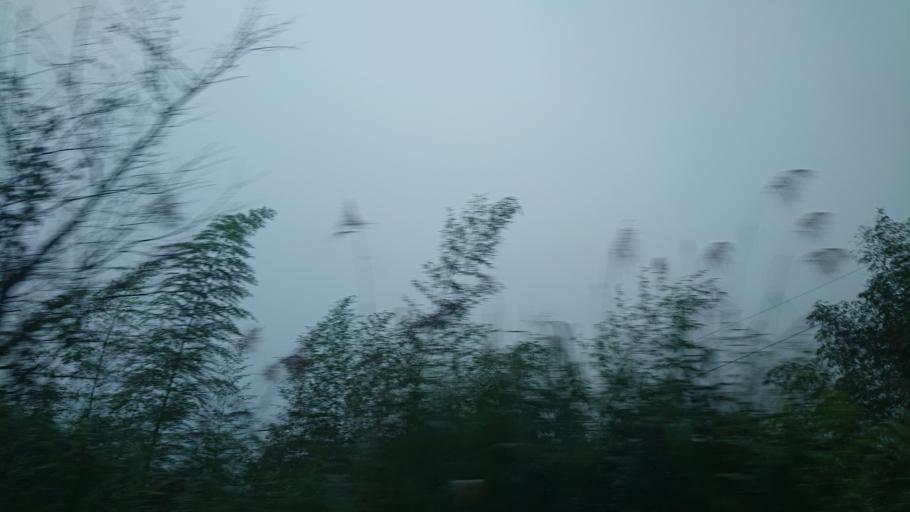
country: TW
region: Taiwan
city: Lugu
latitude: 23.5146
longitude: 120.7029
